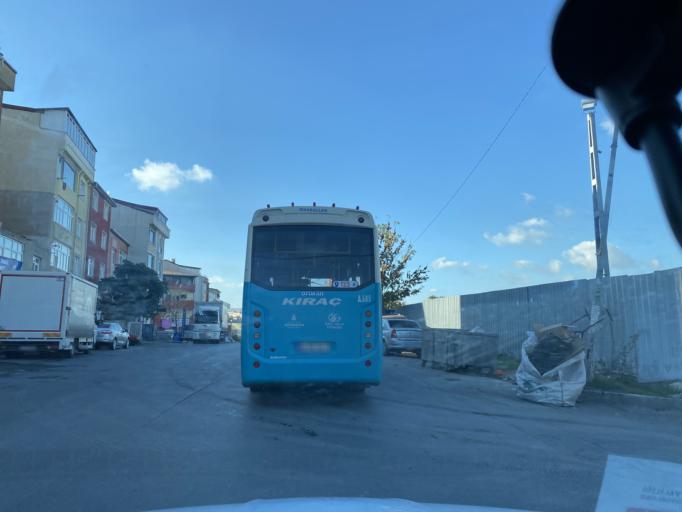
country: TR
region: Istanbul
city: Esenyurt
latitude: 41.0472
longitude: 28.6478
